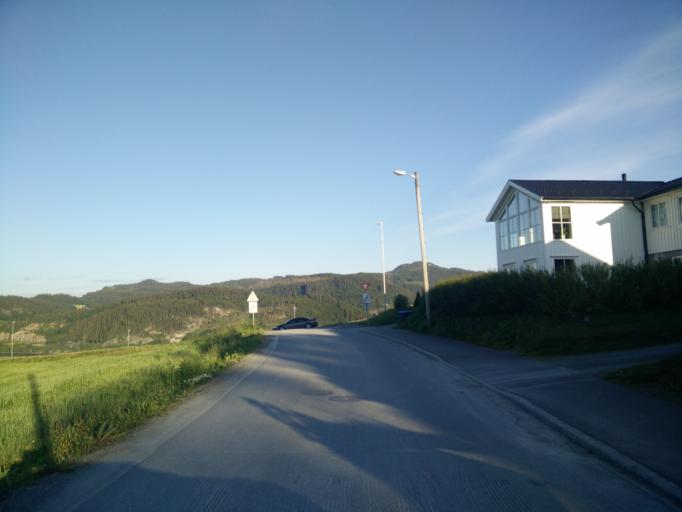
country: NO
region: Sor-Trondelag
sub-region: Skaun
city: Borsa
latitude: 63.3316
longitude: 10.0615
